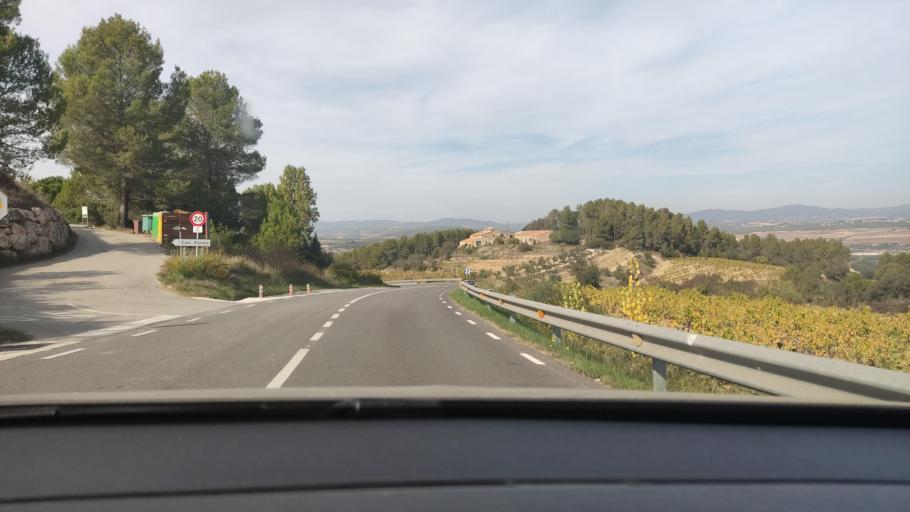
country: ES
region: Catalonia
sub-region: Provincia de Barcelona
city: Sant Sadurni d'Anoia
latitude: 41.4093
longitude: 1.8017
